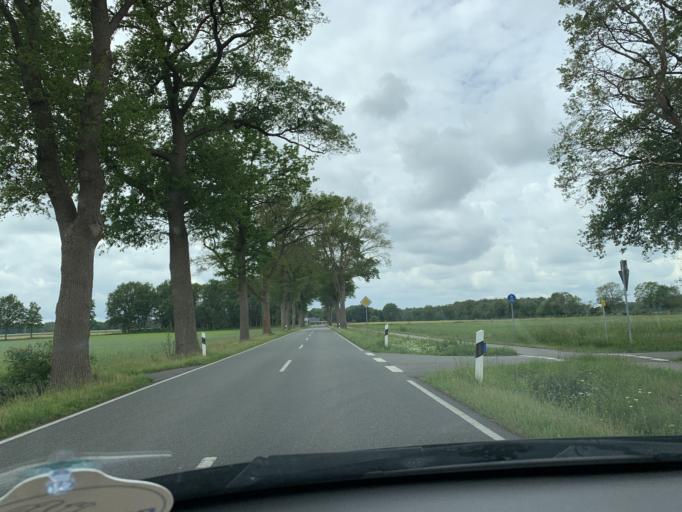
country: DE
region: Lower Saxony
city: Westerstede
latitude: 53.2942
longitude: 7.9914
